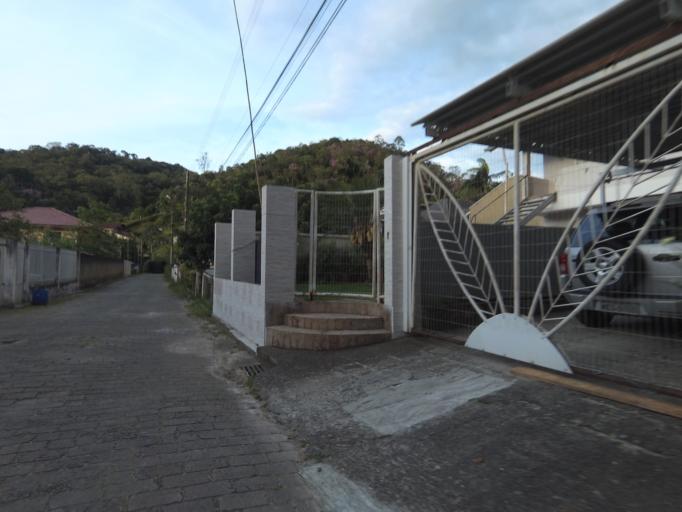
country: BR
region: Santa Catarina
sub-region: Blumenau
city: Blumenau
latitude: -26.9281
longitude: -49.0472
